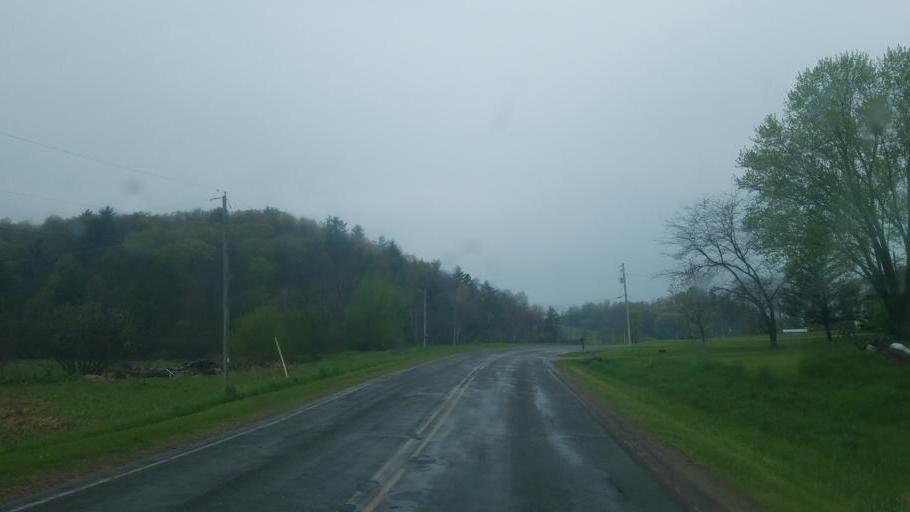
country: US
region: Wisconsin
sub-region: Juneau County
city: Elroy
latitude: 43.6538
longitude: -90.2318
